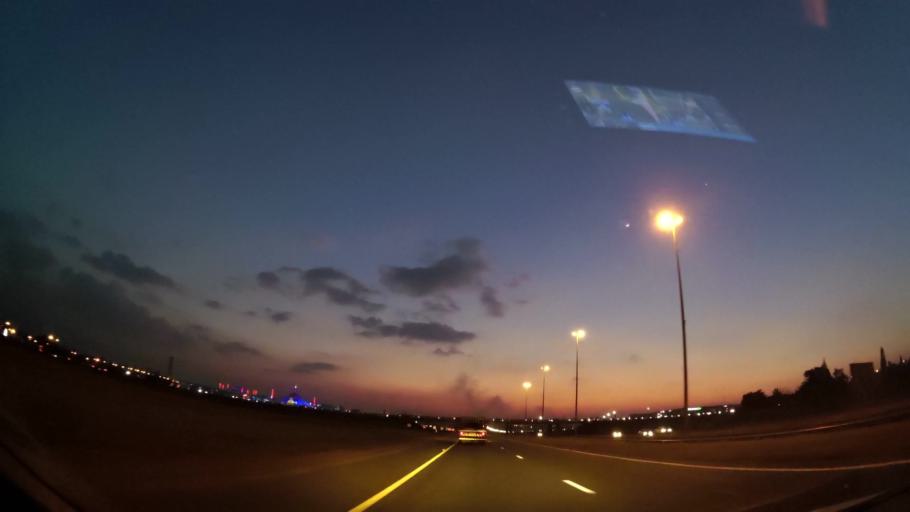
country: ZA
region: Gauteng
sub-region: Ekurhuleni Metropolitan Municipality
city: Brakpan
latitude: -26.2558
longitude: 28.3240
